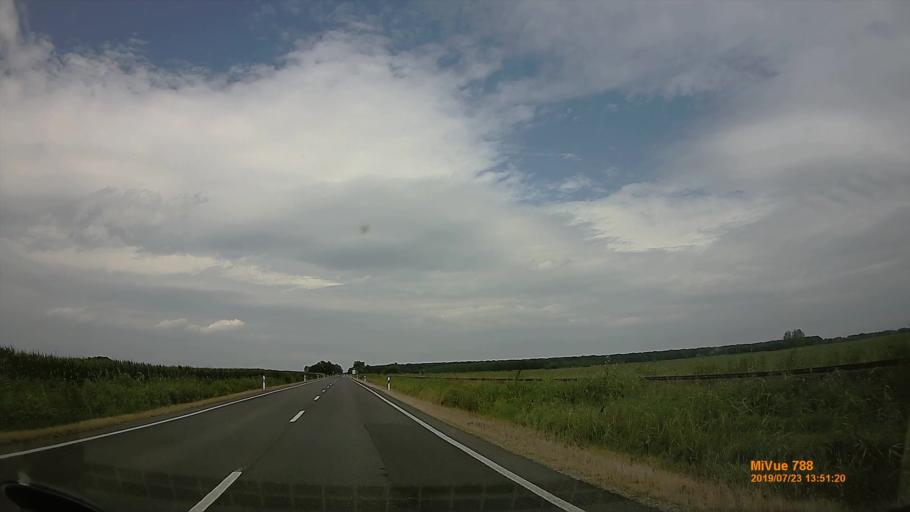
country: HU
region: Hajdu-Bihar
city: Polgar
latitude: 47.8867
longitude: 21.1501
